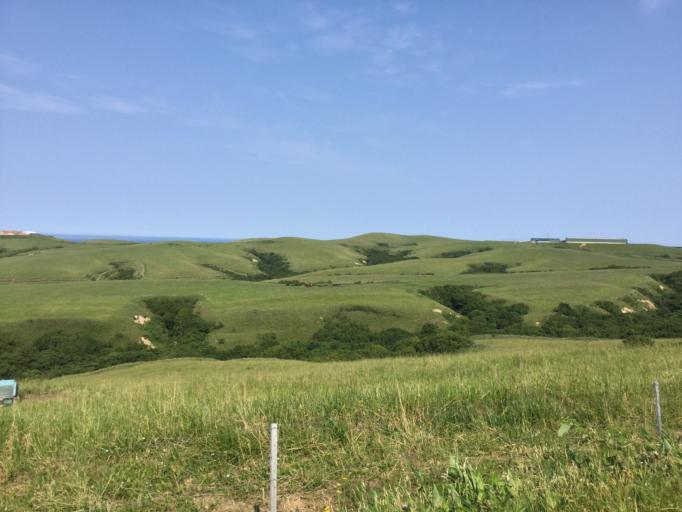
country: JP
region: Hokkaido
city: Makubetsu
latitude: 45.4966
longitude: 141.9176
